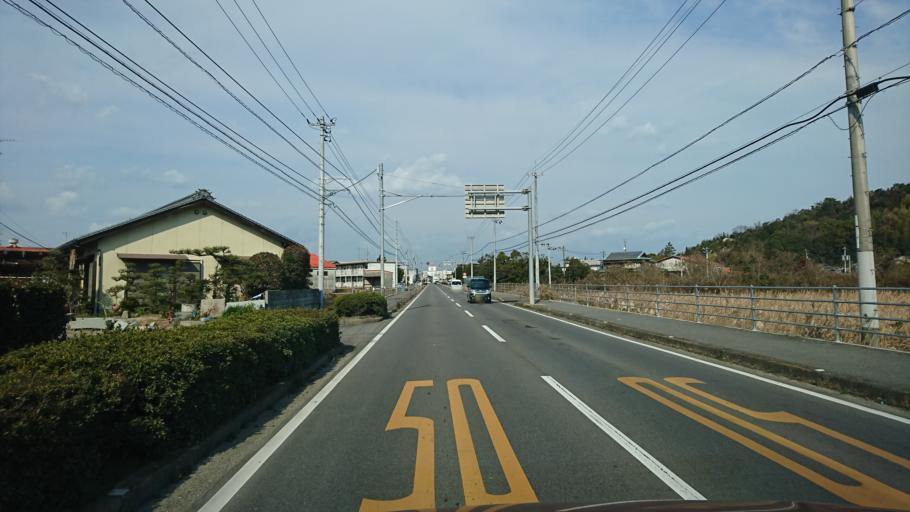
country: JP
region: Ehime
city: Saijo
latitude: 34.0095
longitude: 133.0386
